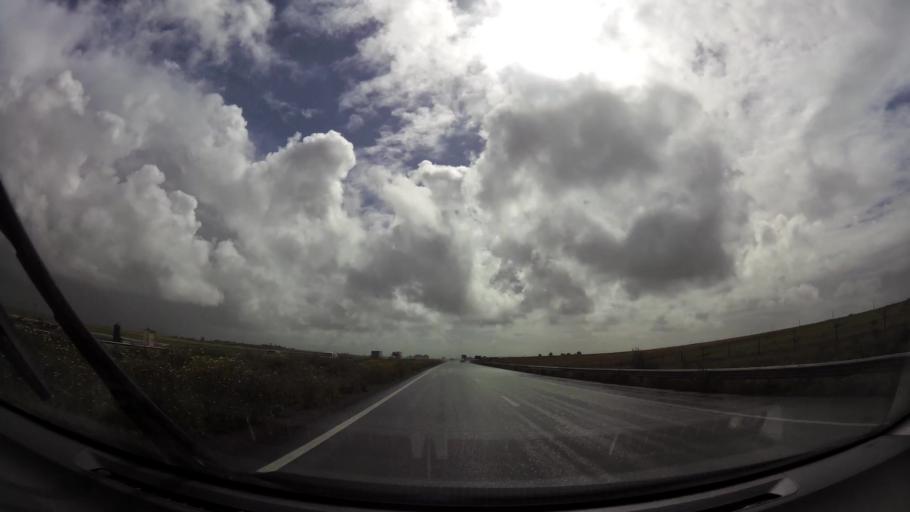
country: MA
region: Grand Casablanca
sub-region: Nouaceur
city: Dar Bouazza
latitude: 33.3807
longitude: -7.8968
